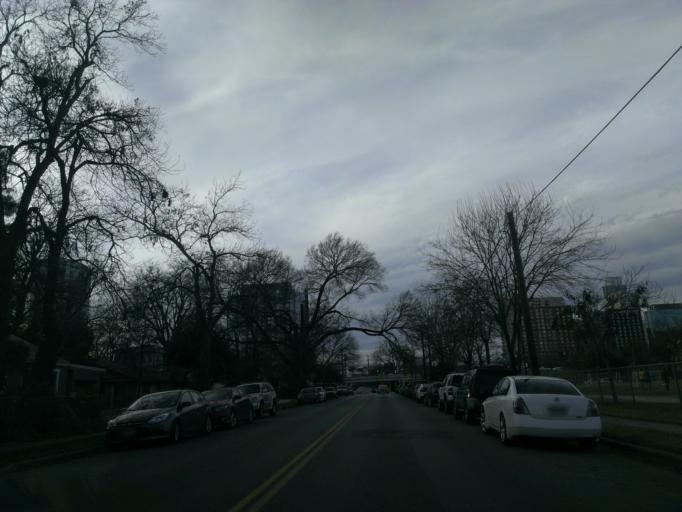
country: US
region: Texas
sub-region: Travis County
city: Austin
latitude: 30.2567
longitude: -97.7350
